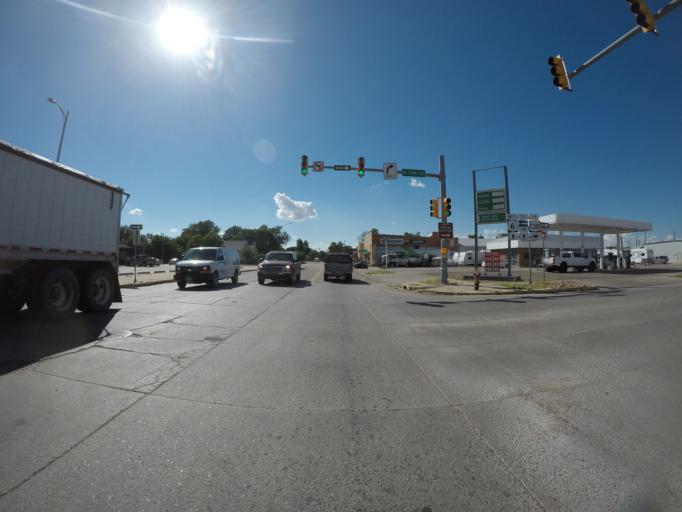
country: US
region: Colorado
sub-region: Logan County
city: Sterling
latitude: 40.6263
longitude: -103.2065
